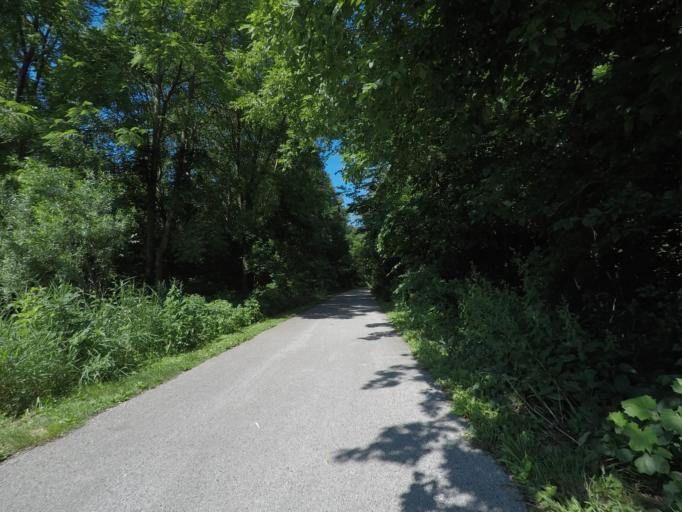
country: US
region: Wisconsin
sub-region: Milwaukee County
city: West Milwaukee
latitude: 43.0245
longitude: -87.9815
